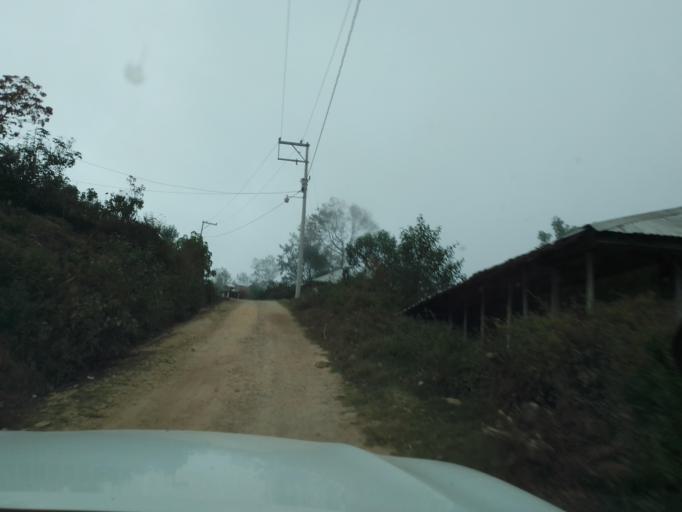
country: MX
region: Chiapas
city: Motozintla de Mendoza
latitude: 15.2216
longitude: -92.2217
